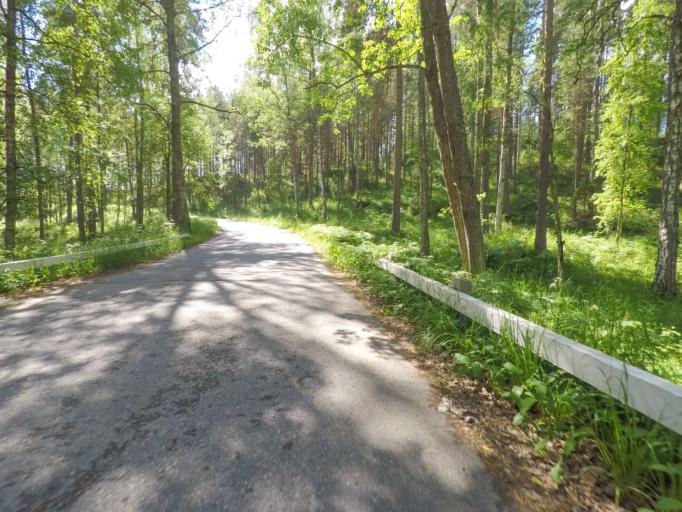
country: FI
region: Southern Savonia
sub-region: Savonlinna
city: Punkaharju
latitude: 61.8033
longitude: 29.3089
